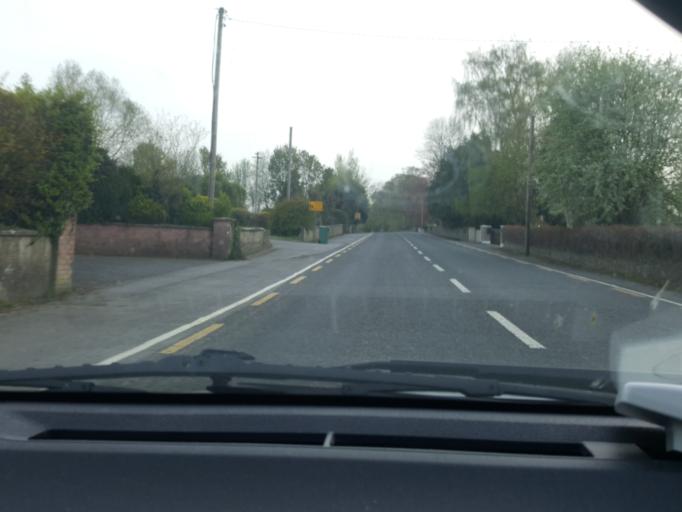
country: IE
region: Munster
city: Cahir
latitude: 52.3843
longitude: -7.9165
